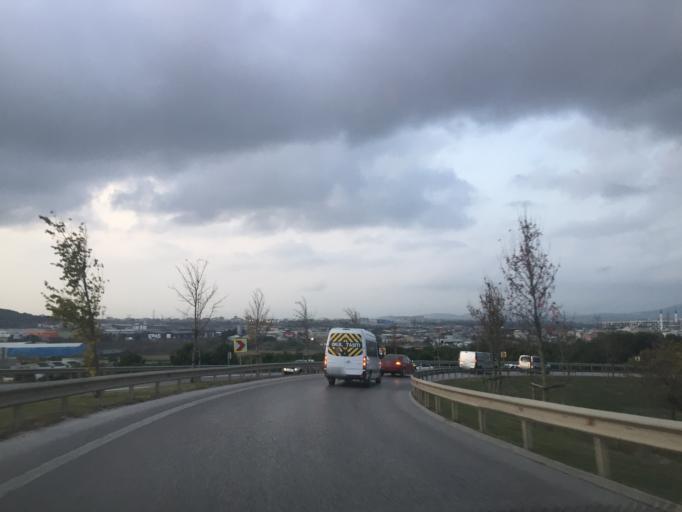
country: TR
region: Istanbul
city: Samandira
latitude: 40.9688
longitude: 29.2159
